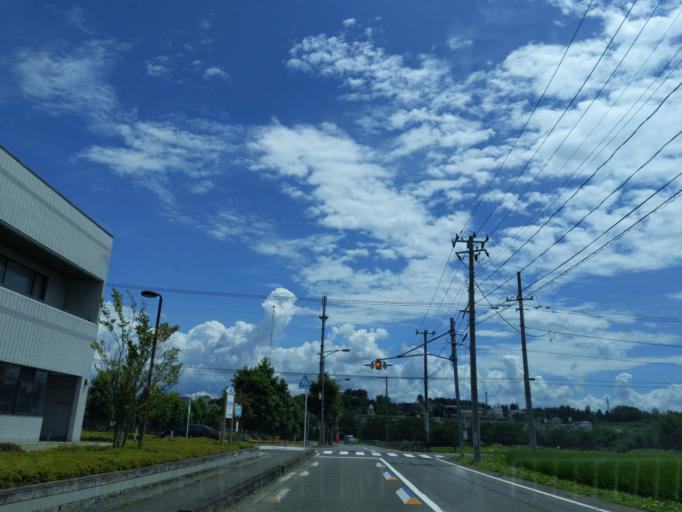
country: JP
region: Fukushima
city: Koriyama
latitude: 37.3653
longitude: 140.3520
